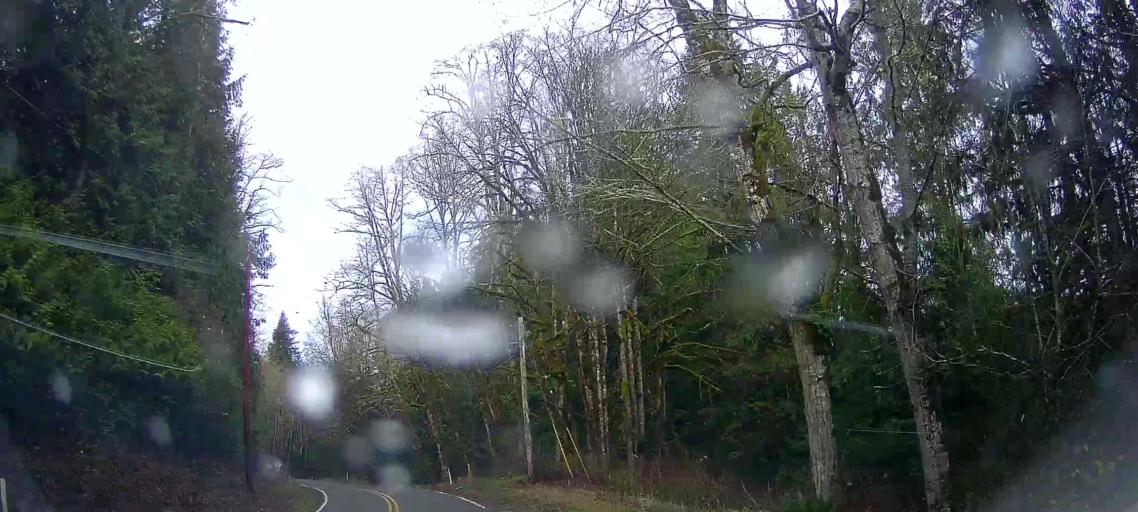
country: US
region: Washington
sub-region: Skagit County
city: Clear Lake
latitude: 48.4794
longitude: -122.1372
